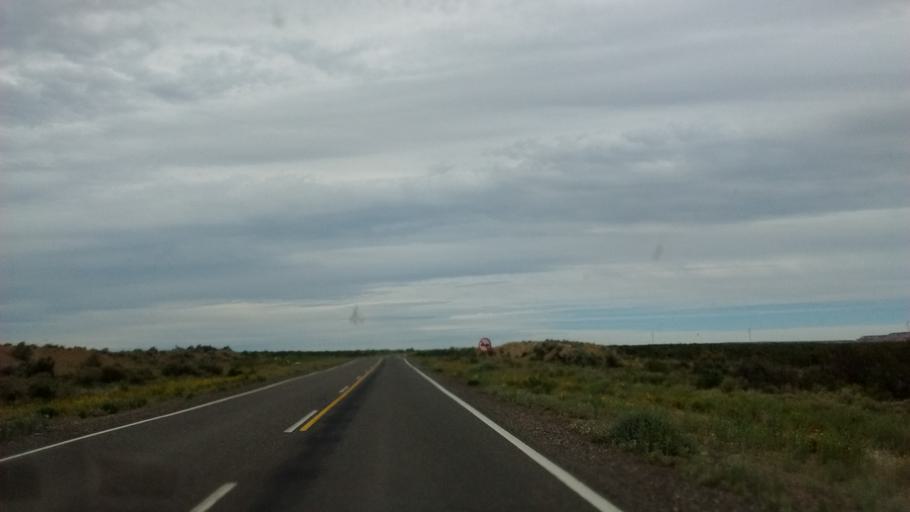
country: AR
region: Rio Negro
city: Catriel
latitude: -38.1210
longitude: -67.9314
